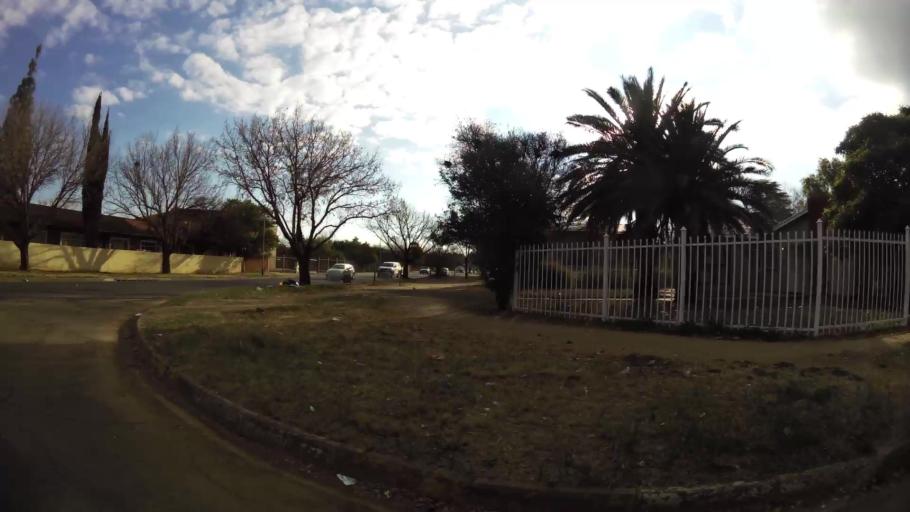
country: ZA
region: Orange Free State
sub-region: Mangaung Metropolitan Municipality
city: Bloemfontein
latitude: -29.1014
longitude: 26.1913
